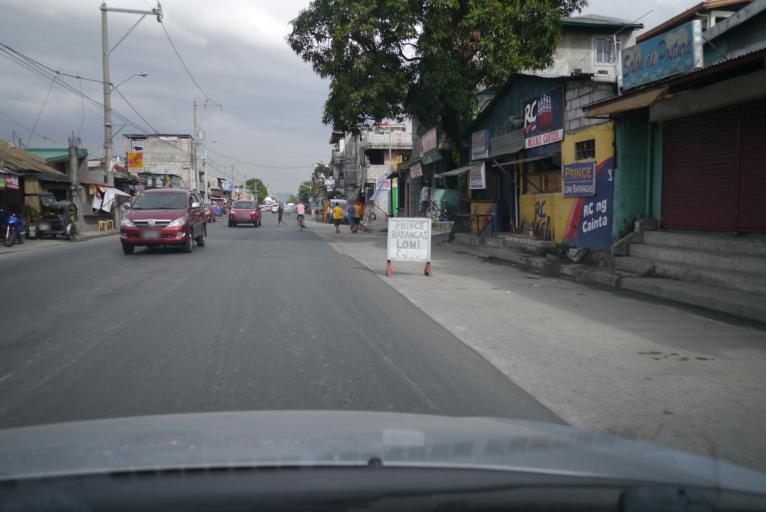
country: PH
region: Calabarzon
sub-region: Province of Rizal
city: Cainta
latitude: 14.5614
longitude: 121.1121
